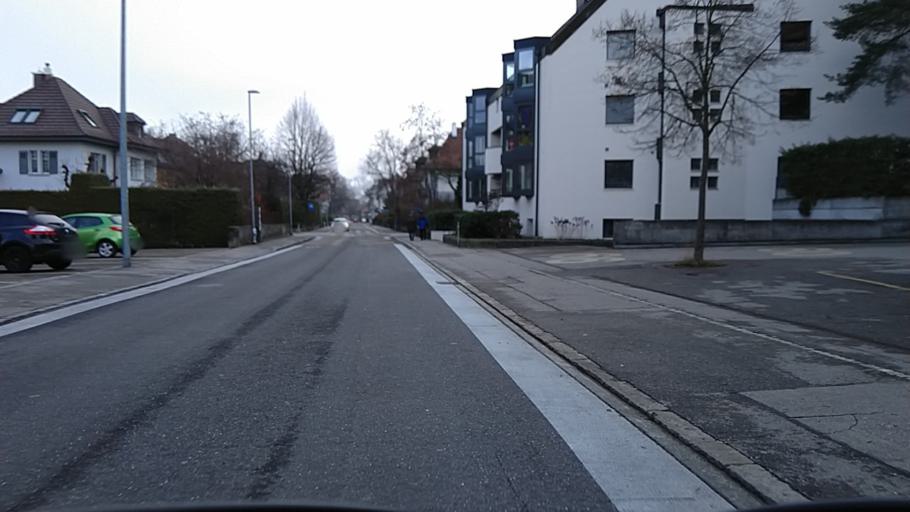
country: CH
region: Bern
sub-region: Bern-Mittelland District
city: Koniz
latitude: 46.9433
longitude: 7.3864
